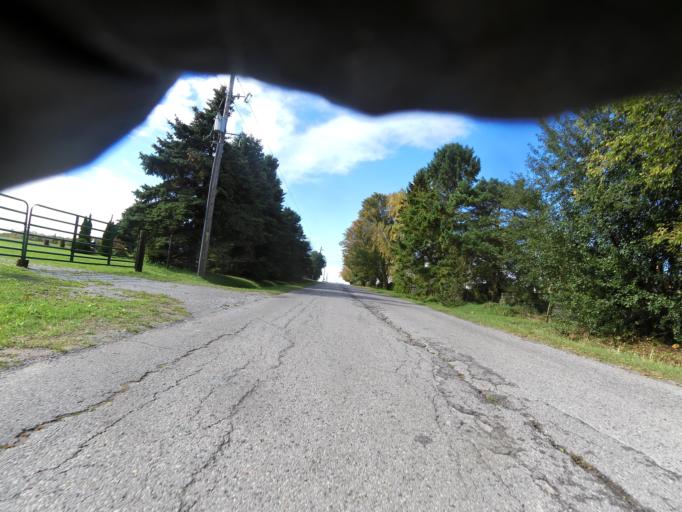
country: CA
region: Ontario
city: Cobourg
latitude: 43.9384
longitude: -78.3430
